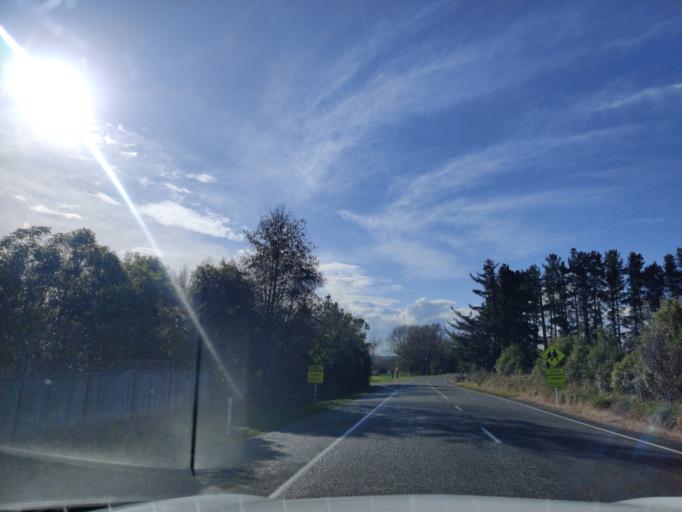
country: NZ
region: Manawatu-Wanganui
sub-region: Palmerston North City
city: Palmerston North
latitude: -40.3662
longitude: 175.6638
